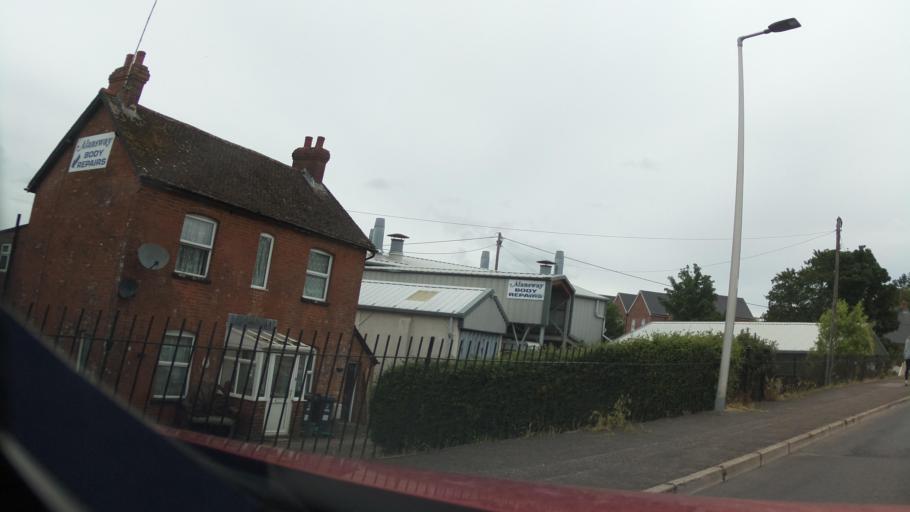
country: GB
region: England
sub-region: Devon
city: Ottery St Mary
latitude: 50.7486
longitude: -3.2868
